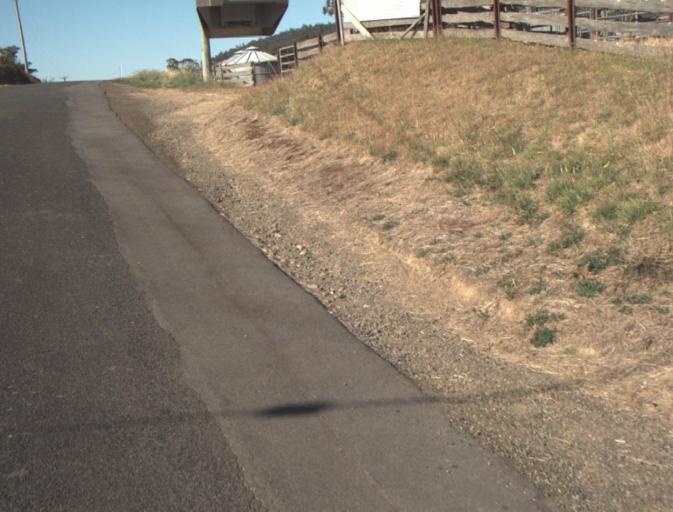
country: AU
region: Tasmania
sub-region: Launceston
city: Newstead
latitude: -41.3445
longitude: 147.3032
